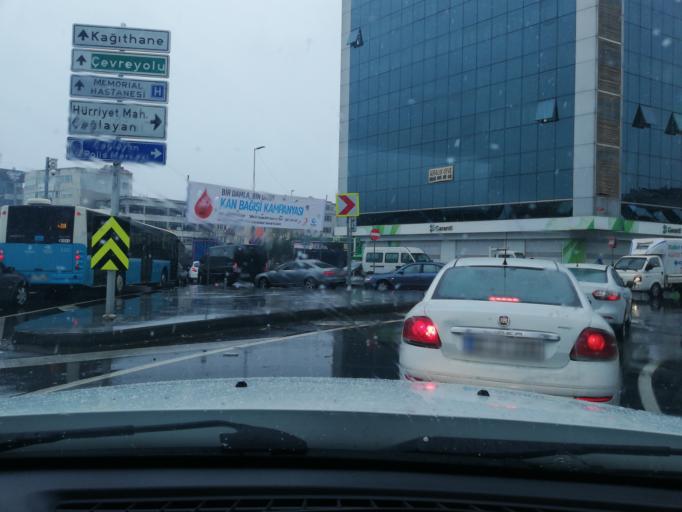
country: TR
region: Istanbul
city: Sisli
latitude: 41.0709
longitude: 28.9806
